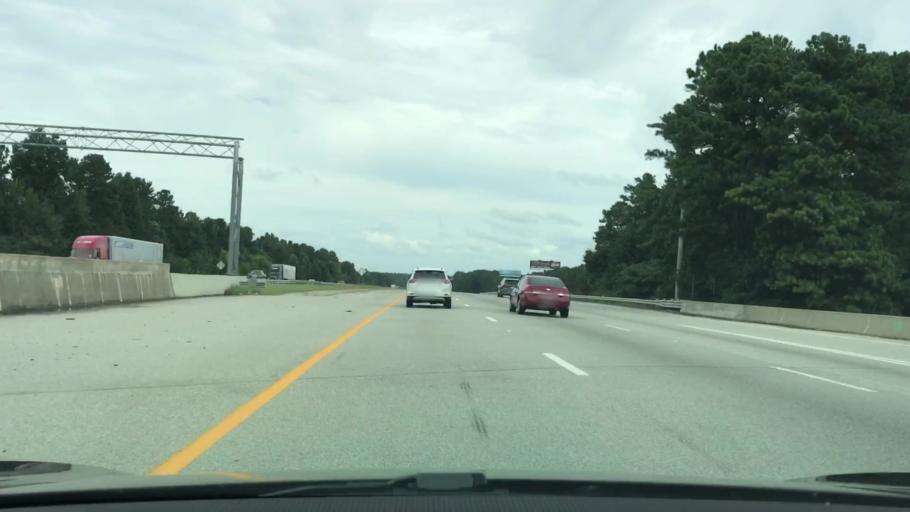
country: US
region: Georgia
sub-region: Coweta County
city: Grantville
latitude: 33.2424
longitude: -84.8065
